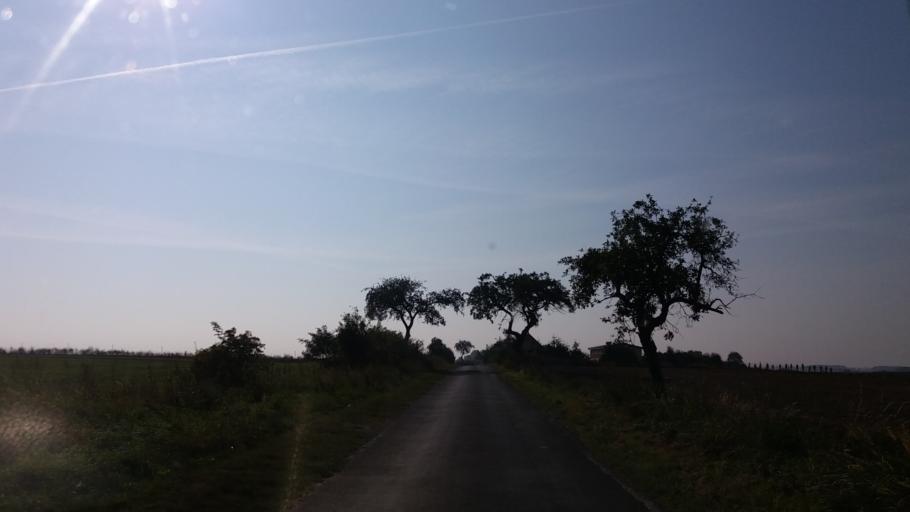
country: PL
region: West Pomeranian Voivodeship
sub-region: Powiat choszczenski
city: Pelczyce
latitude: 53.0252
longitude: 15.3258
